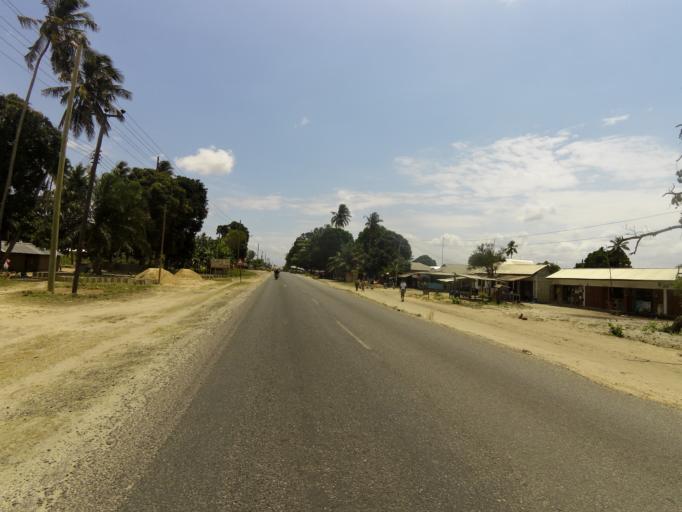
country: TZ
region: Pwani
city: Vikindu
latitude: -7.0331
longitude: 39.2835
